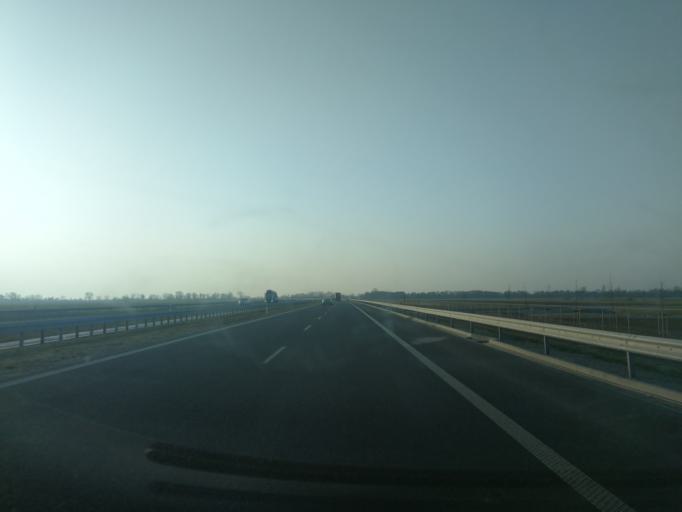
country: PL
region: Pomeranian Voivodeship
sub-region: Powiat malborski
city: Stare Pole
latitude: 54.1699
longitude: 19.2250
